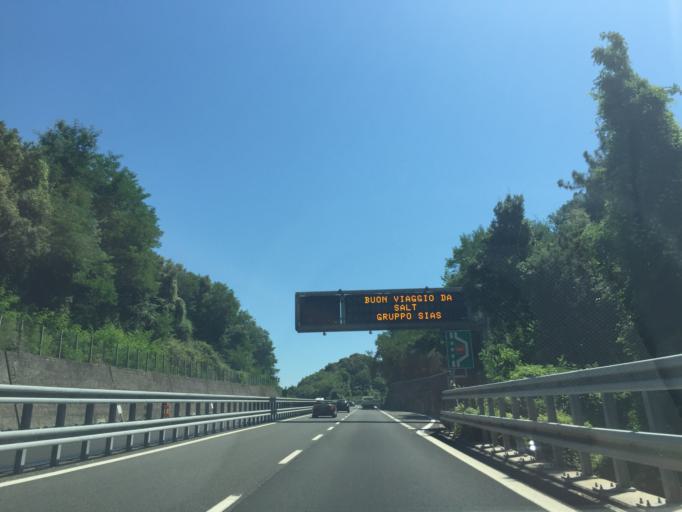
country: IT
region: Tuscany
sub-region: Provincia di Lucca
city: Massarosa
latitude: 43.8625
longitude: 10.3669
